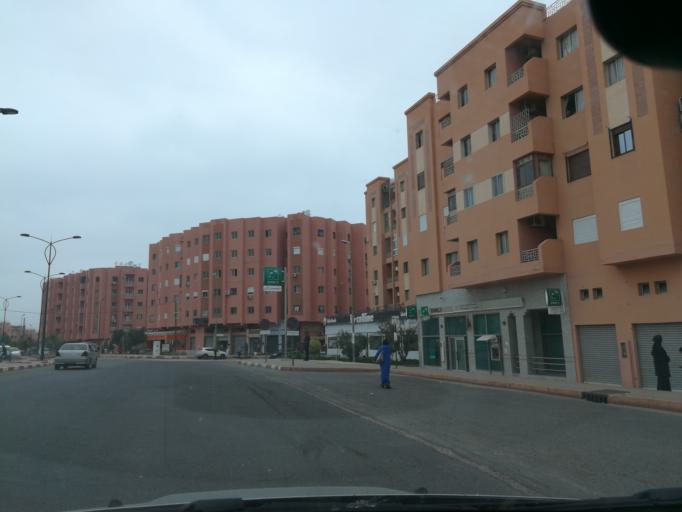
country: MA
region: Marrakech-Tensift-Al Haouz
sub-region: Marrakech
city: Marrakesh
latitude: 31.6715
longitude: -8.0140
